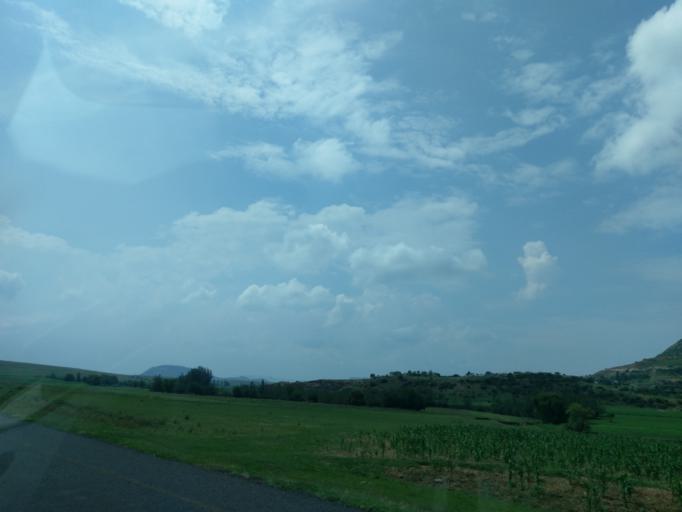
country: LS
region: Leribe
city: Leribe
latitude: -29.0070
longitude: 27.9961
